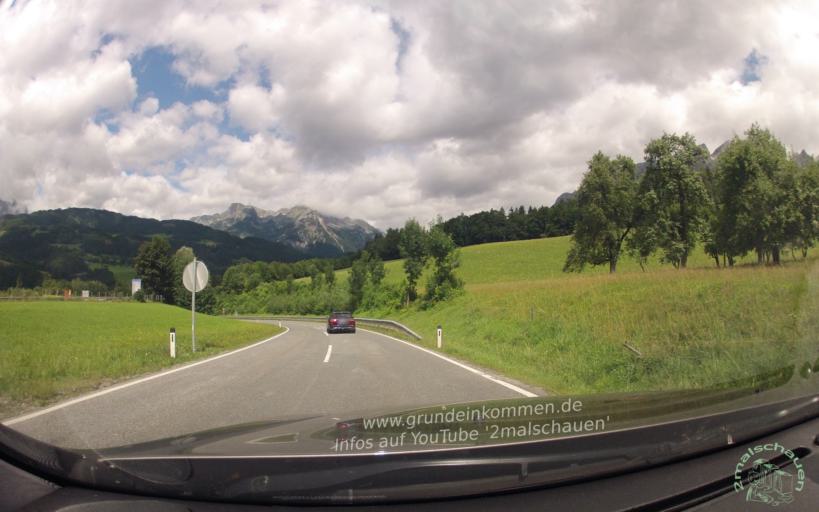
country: AT
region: Salzburg
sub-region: Politischer Bezirk Sankt Johann im Pongau
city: Pfarrwerfen
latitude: 47.4588
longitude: 13.2110
